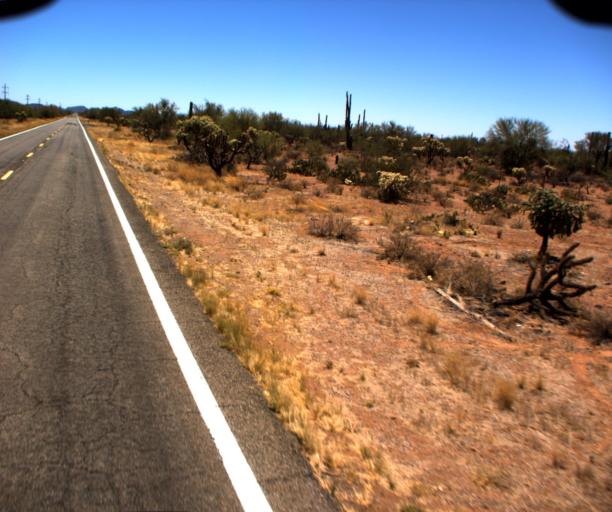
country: US
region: Arizona
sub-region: Pima County
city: Sells
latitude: 32.0507
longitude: -112.0259
